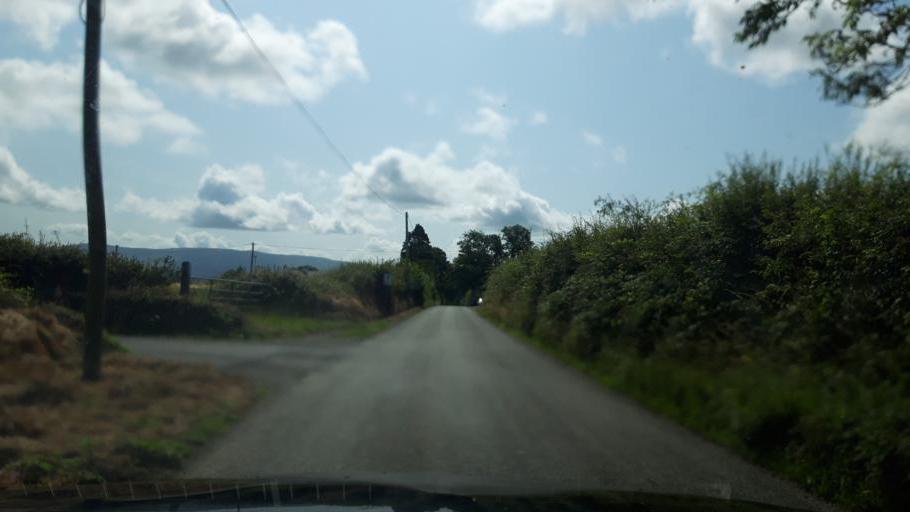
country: IE
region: Leinster
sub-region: Kilkenny
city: Graiguenamanagh
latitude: 52.5522
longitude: -6.9743
